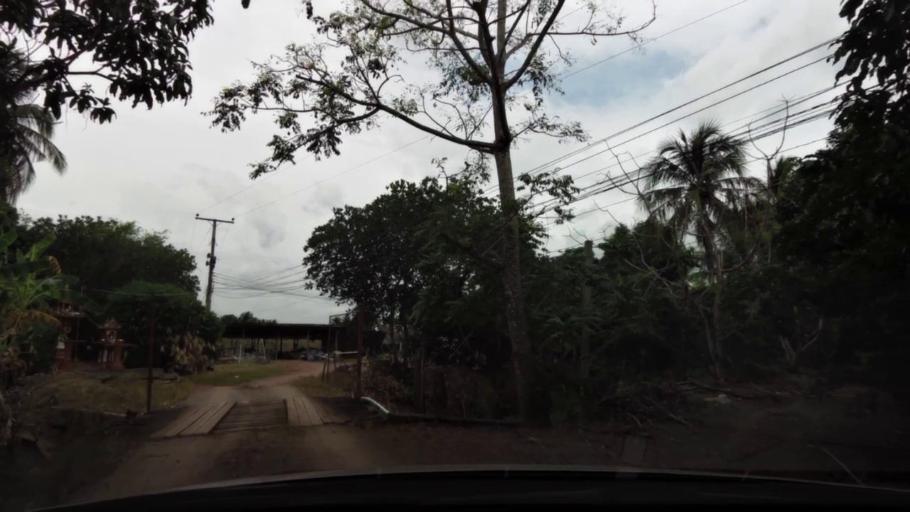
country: TH
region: Ratchaburi
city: Damnoen Saduak
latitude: 13.5711
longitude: 100.0020
